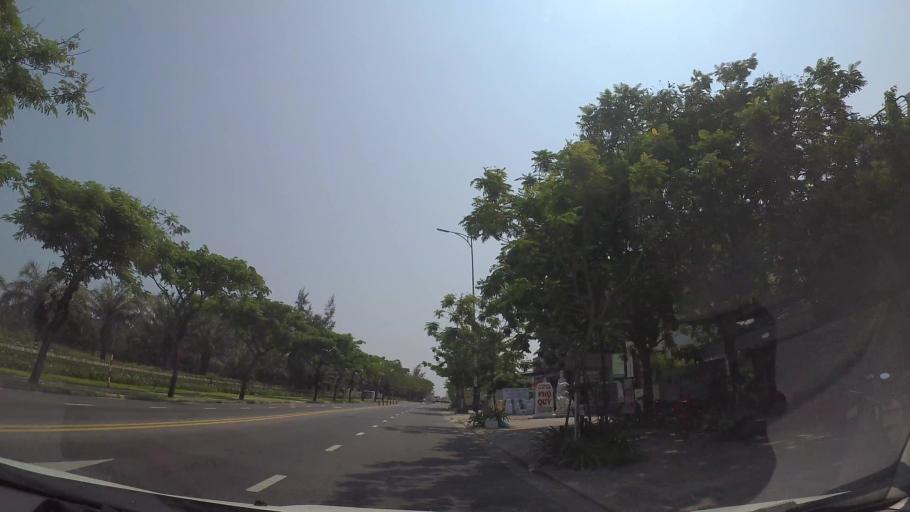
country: VN
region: Da Nang
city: Ngu Hanh Son
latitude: 16.0011
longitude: 108.2673
